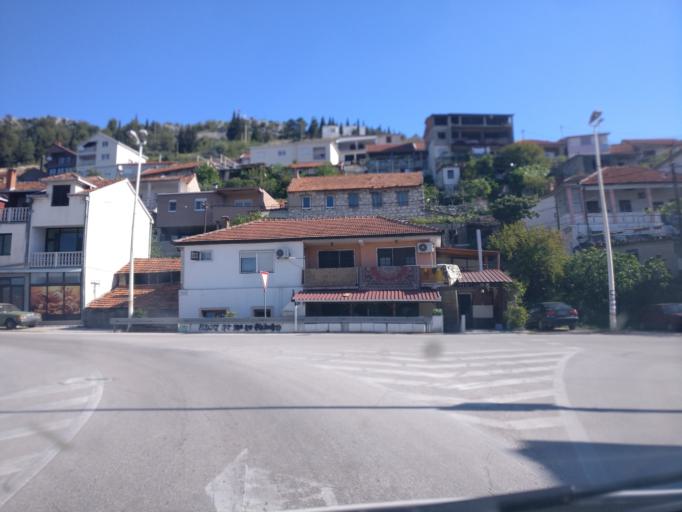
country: BA
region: Federation of Bosnia and Herzegovina
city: Tasovcici
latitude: 43.1149
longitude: 17.7020
